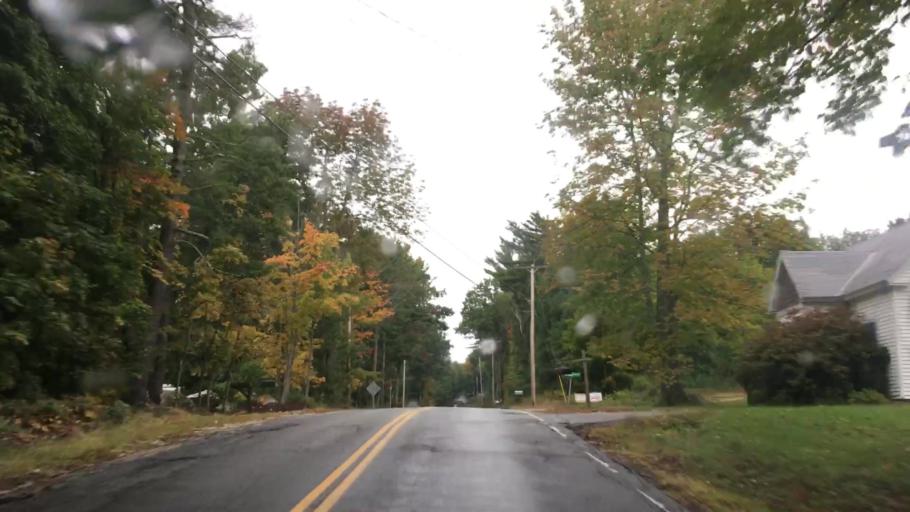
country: US
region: Maine
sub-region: Cumberland County
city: New Gloucester
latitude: 43.9255
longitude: -70.3676
